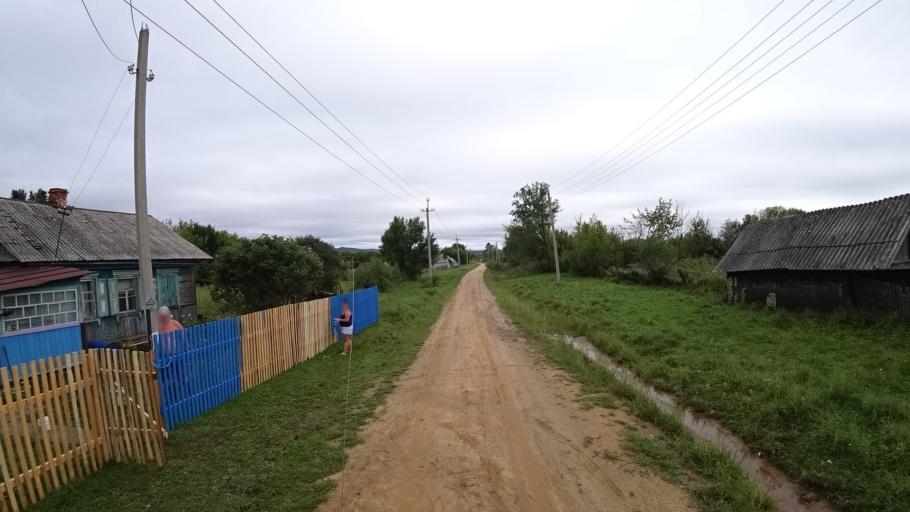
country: RU
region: Primorskiy
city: Rettikhovka
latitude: 44.1415
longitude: 132.6412
